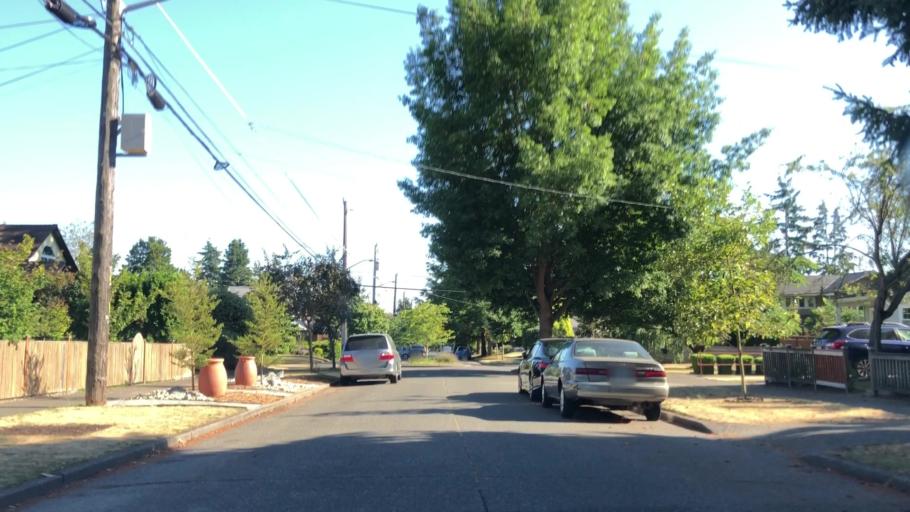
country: US
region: Washington
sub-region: King County
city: Shoreline
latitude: 47.6892
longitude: -122.3741
